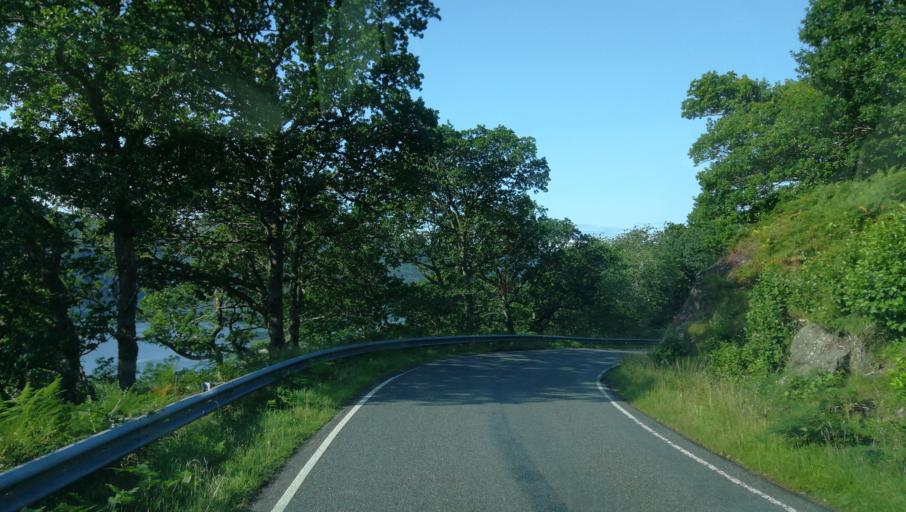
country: GB
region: Scotland
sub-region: Argyll and Bute
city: Isle Of Mull
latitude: 56.6811
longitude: -5.8279
